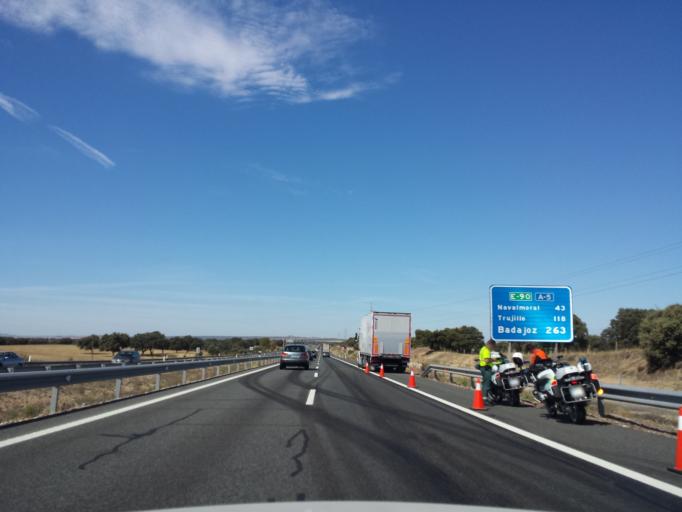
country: ES
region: Castille-La Mancha
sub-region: Province of Toledo
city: Alcanizo
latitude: 39.9204
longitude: -5.0441
